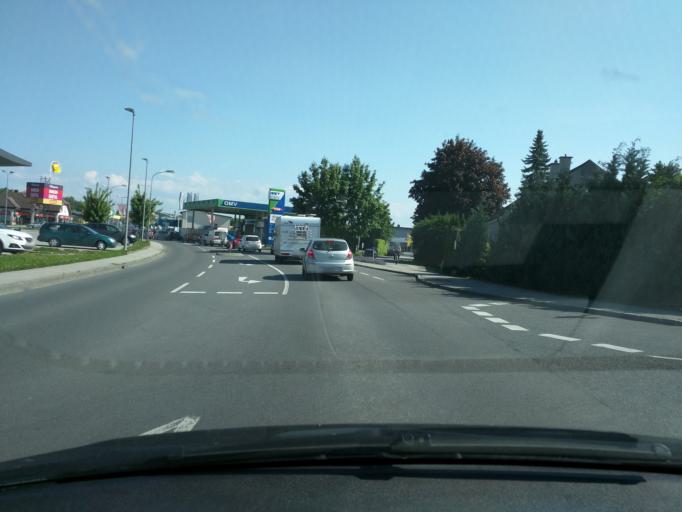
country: AT
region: Lower Austria
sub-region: Politischer Bezirk Melk
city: Ybbs an der Donau
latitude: 48.1721
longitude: 15.0841
